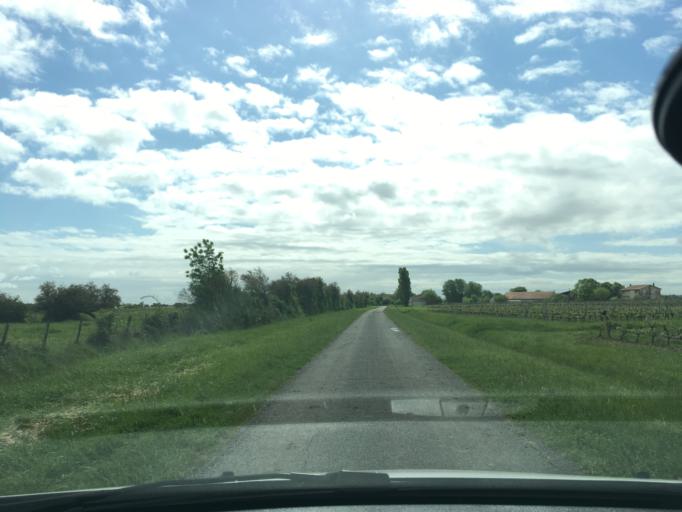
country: FR
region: Aquitaine
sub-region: Departement de la Gironde
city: Saint-Estephe
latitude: 45.3263
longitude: -0.8033
